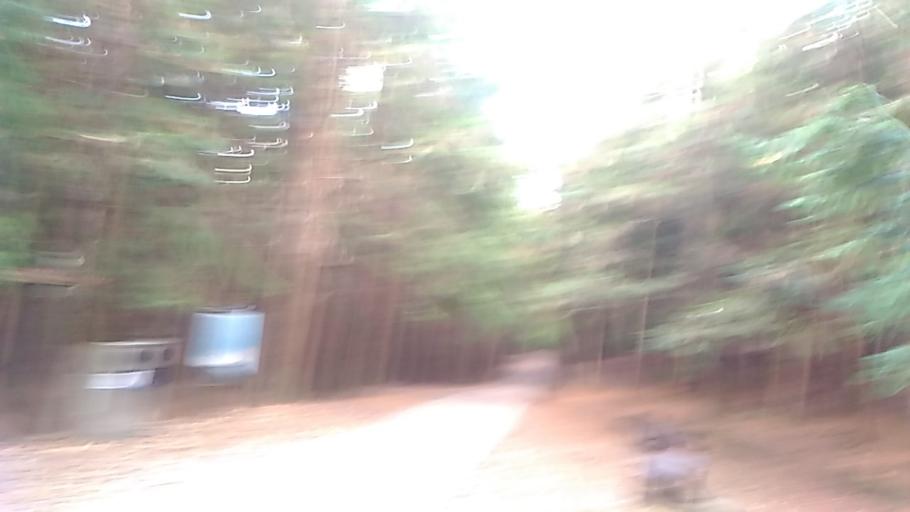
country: TW
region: Taiwan
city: Daxi
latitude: 24.4050
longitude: 121.3073
